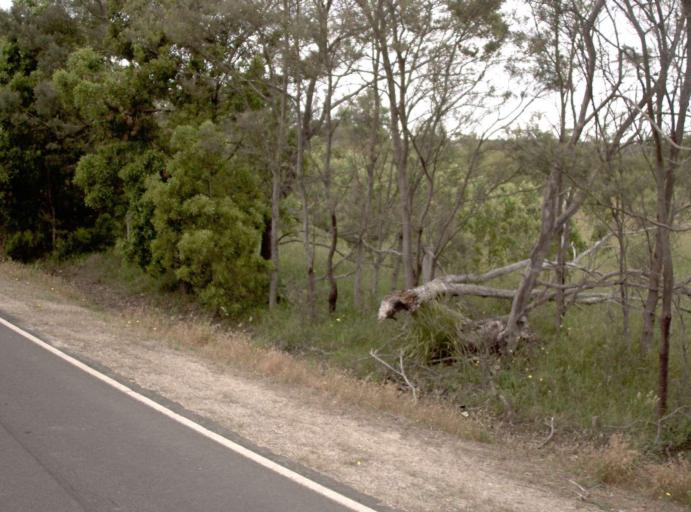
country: AU
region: Victoria
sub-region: Latrobe
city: Traralgon
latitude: -38.4860
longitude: 146.8201
